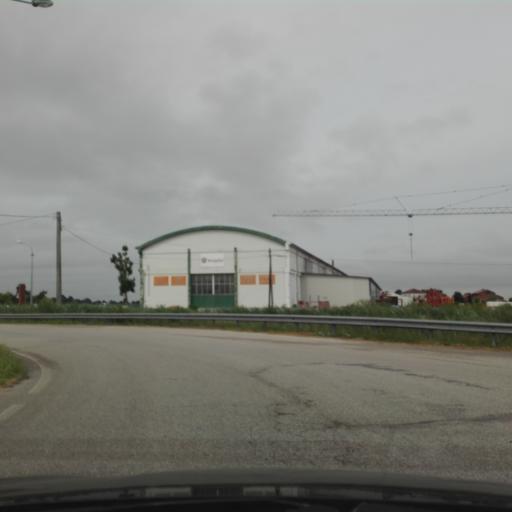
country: IT
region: Veneto
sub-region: Provincia di Rovigo
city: Rovigo
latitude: 45.0776
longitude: 11.7662
